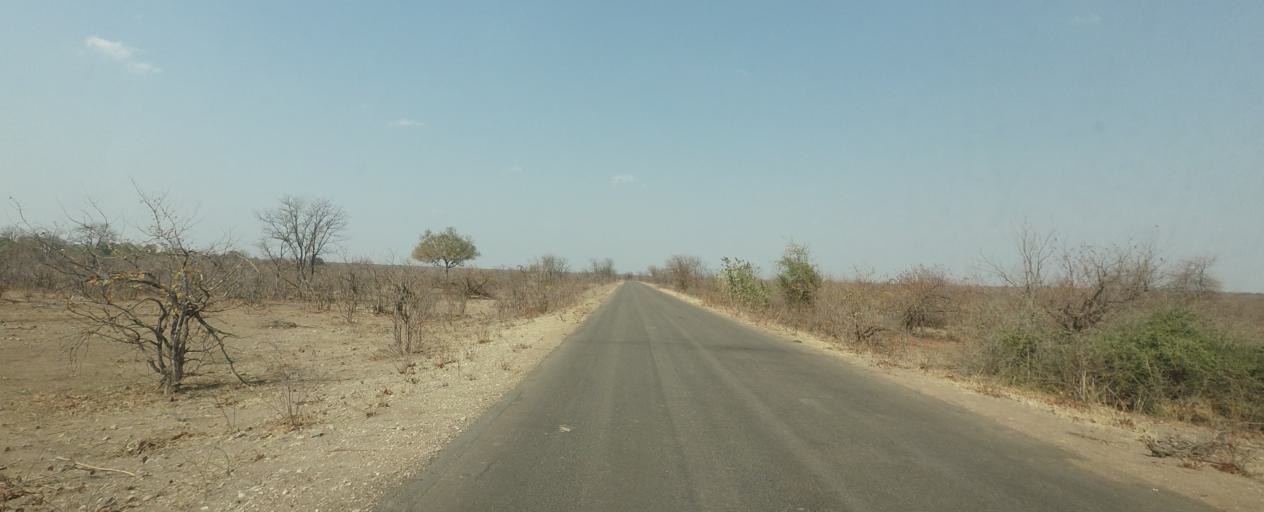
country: ZA
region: Limpopo
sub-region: Mopani District Municipality
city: Giyani
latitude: -23.1676
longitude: 31.3411
